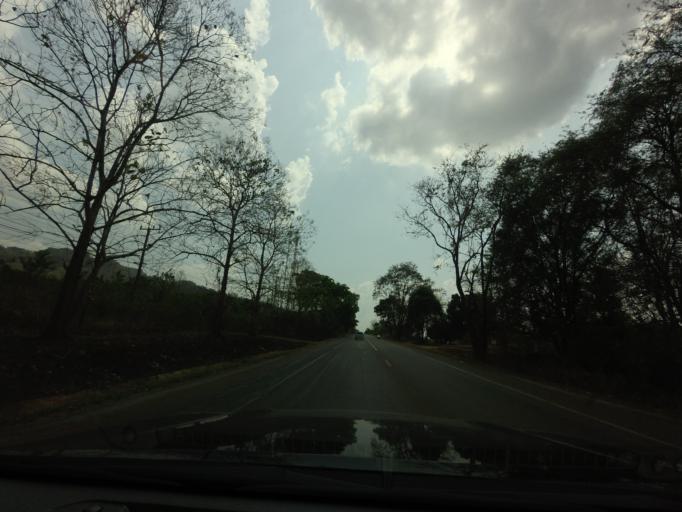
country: TH
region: Kanchanaburi
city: Sai Yok
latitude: 14.1568
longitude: 99.1393
